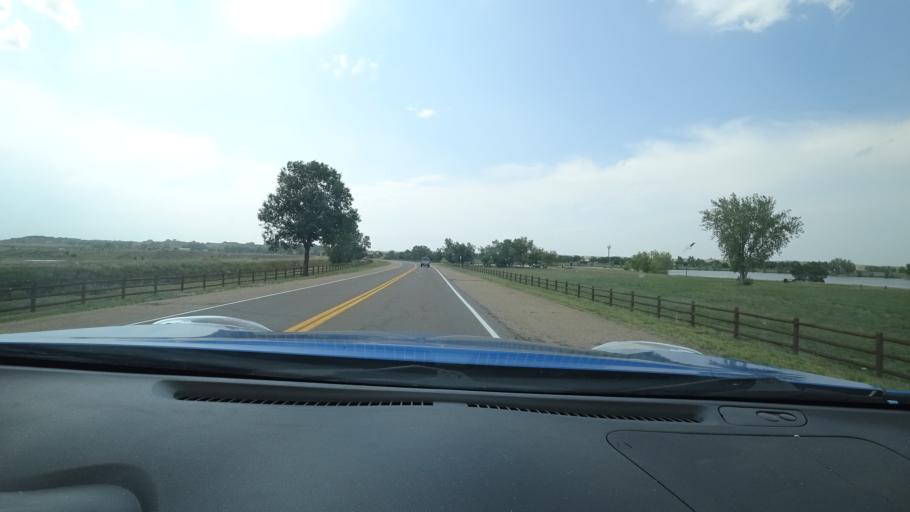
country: US
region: Colorado
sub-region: Adams County
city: Todd Creek
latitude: 39.9236
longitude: -104.8697
